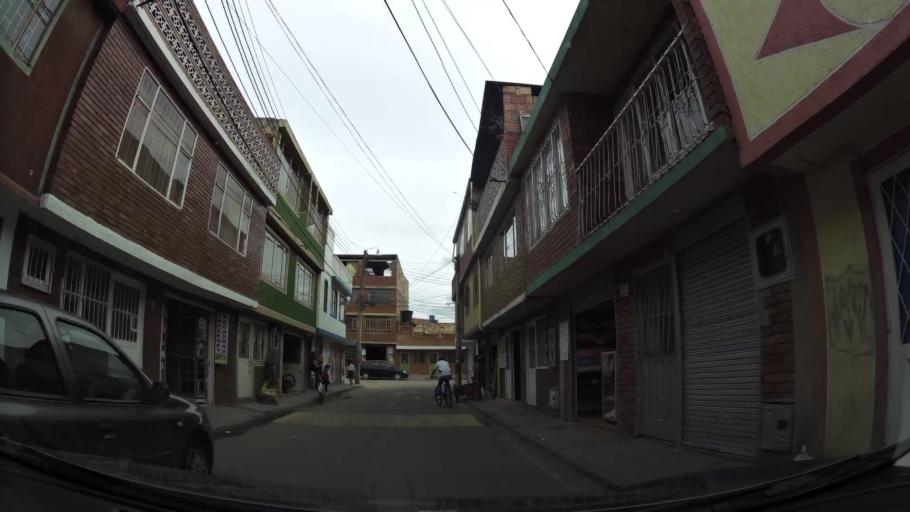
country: CO
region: Cundinamarca
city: Funza
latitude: 4.7103
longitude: -74.2184
